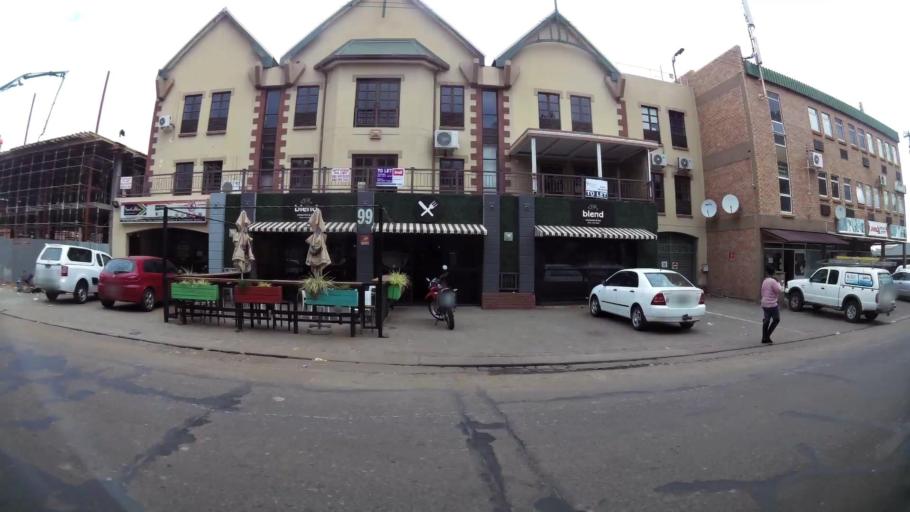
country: ZA
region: Orange Free State
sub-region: Mangaung Metropolitan Municipality
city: Bloemfontein
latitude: -29.1082
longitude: 26.2100
